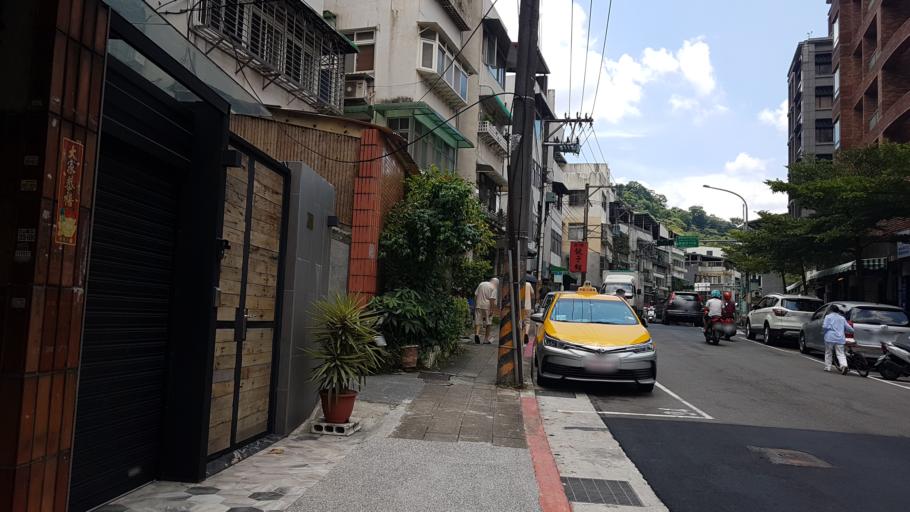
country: TW
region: Taipei
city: Taipei
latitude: 24.9978
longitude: 121.5480
